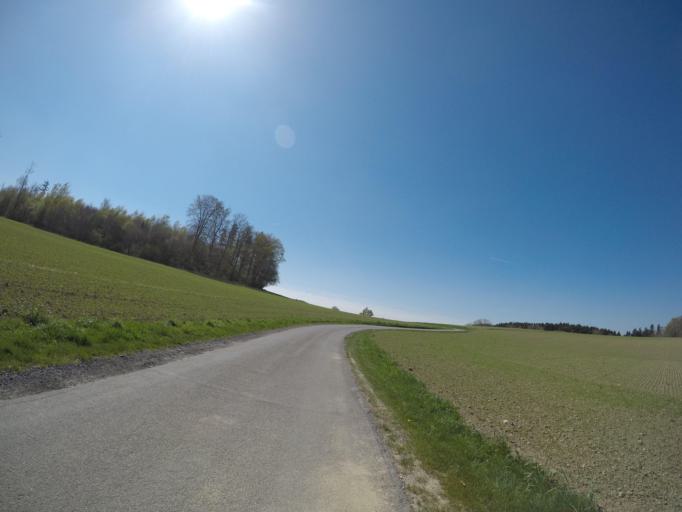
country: DE
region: Baden-Wuerttemberg
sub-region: Tuebingen Region
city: Markdorf
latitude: 47.7593
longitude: 9.3990
